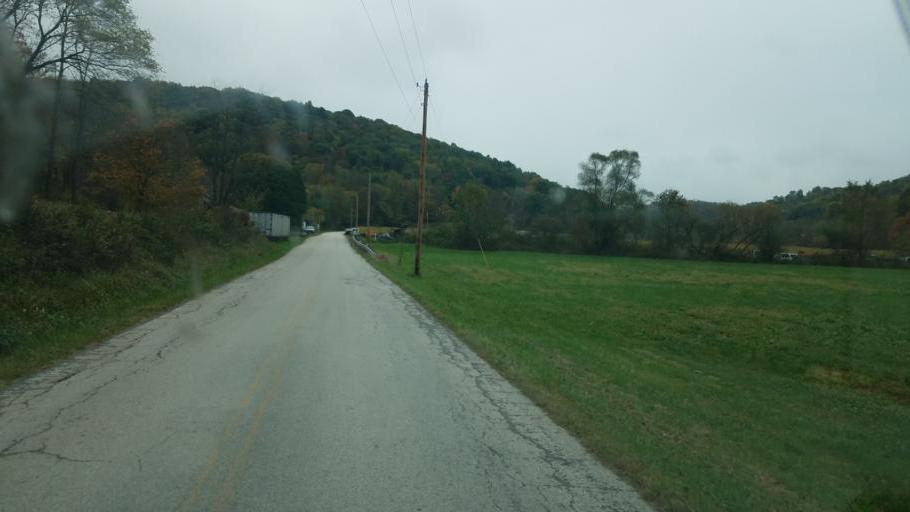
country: US
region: Ohio
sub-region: Ashland County
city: Loudonville
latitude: 40.5316
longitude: -82.1056
